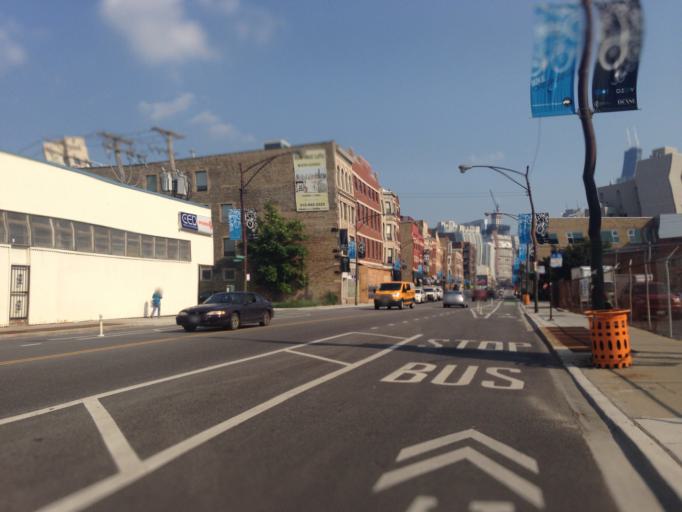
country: US
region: Illinois
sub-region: Cook County
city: Chicago
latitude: 41.8951
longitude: -87.6537
